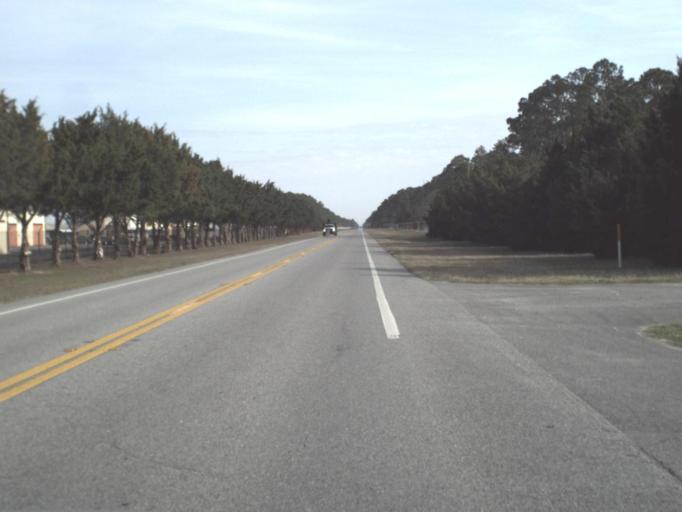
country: US
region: Florida
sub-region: Bay County
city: Tyndall Air Force Base
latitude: 30.0637
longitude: -85.5822
